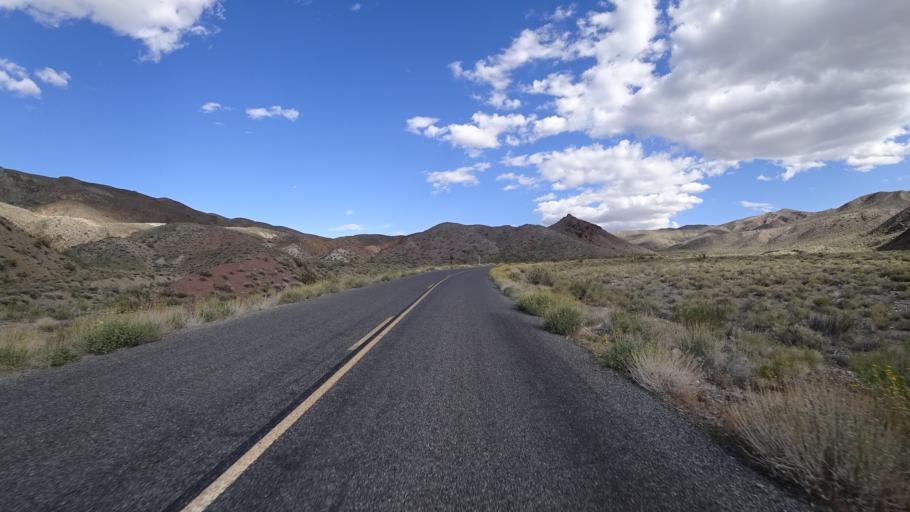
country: US
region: Nevada
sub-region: Nye County
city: Beatty
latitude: 36.4222
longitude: -117.1883
